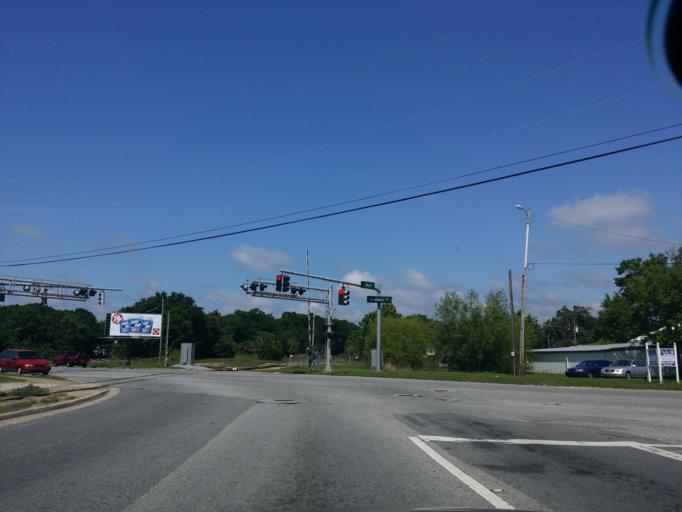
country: US
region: Florida
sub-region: Escambia County
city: Pensacola
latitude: 30.4060
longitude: -87.2374
